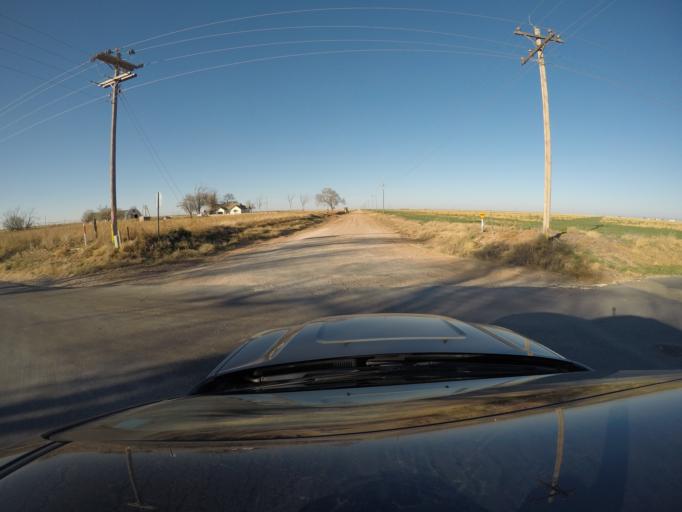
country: US
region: New Mexico
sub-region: Curry County
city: Texico
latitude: 34.3465
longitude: -103.1083
